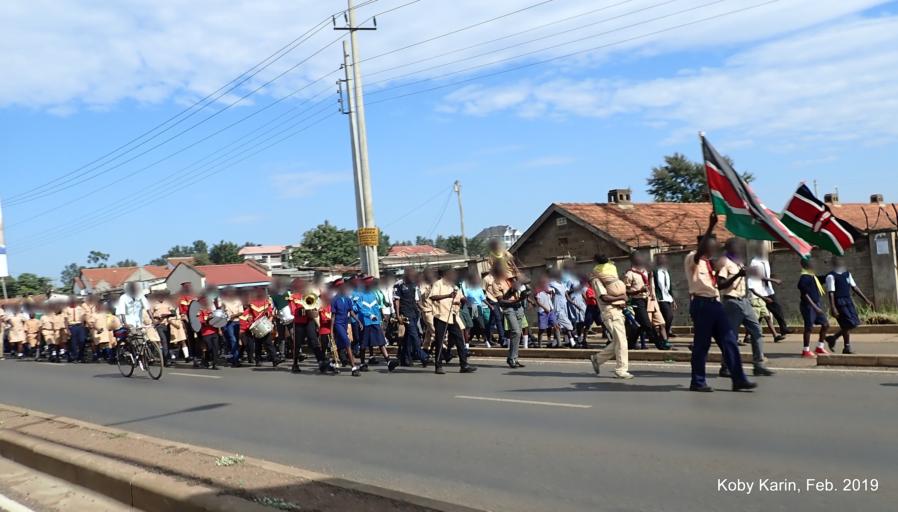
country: KE
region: Kisumu
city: Kisumu
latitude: -0.1073
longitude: 34.7665
